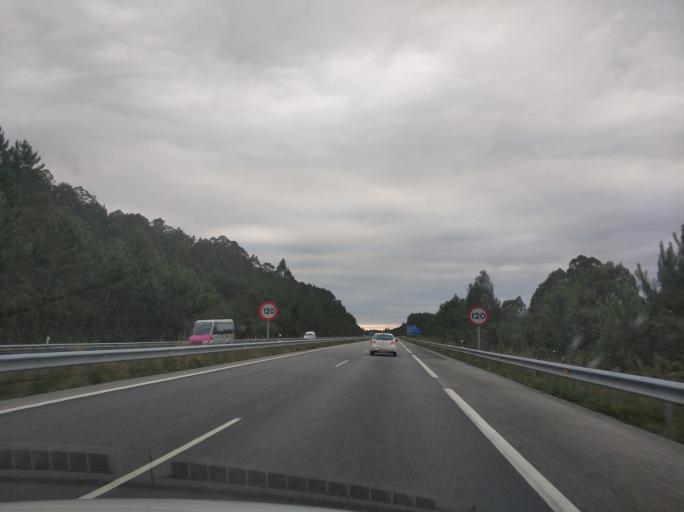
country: ES
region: Asturias
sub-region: Province of Asturias
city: Tineo
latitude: 43.5422
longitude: -6.4287
